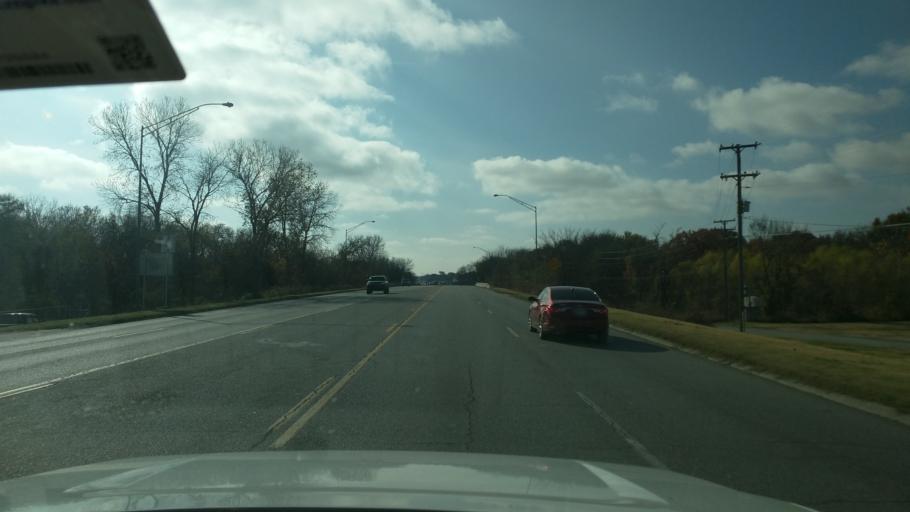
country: US
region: Oklahoma
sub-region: Washington County
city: Dewey
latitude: 36.7841
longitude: -95.9352
